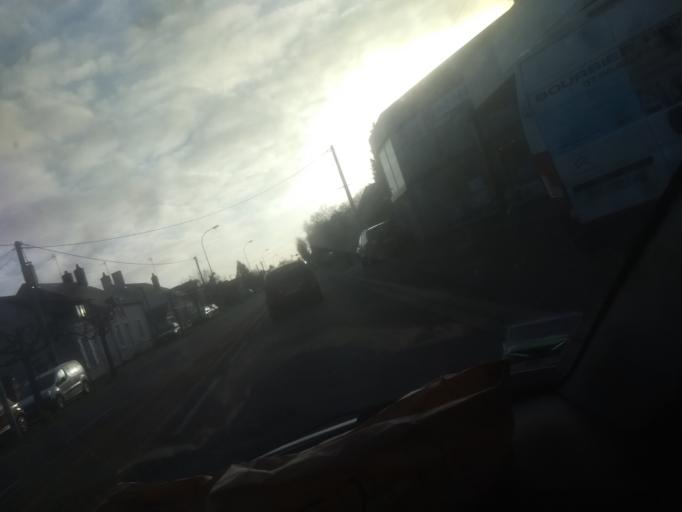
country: FR
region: Centre
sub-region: Departement du Cher
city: Mehun-sur-Yevre
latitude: 47.1439
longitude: 2.2267
